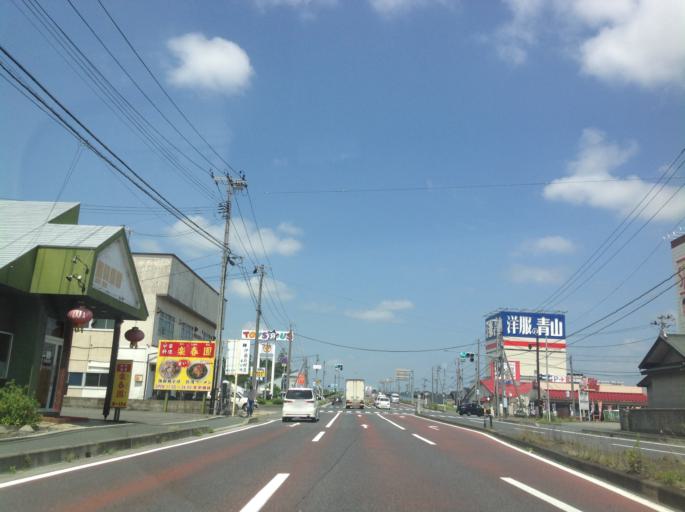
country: JP
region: Iwate
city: Kitakami
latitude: 39.2921
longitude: 141.1051
